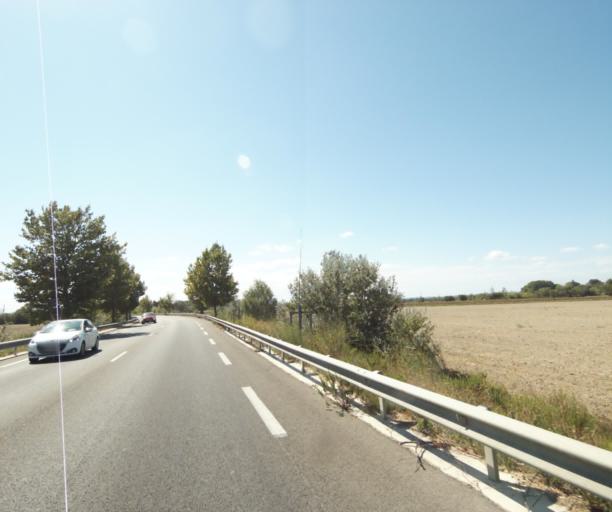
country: FR
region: Languedoc-Roussillon
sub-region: Departement du Gard
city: Rodilhan
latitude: 43.8299
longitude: 4.4222
